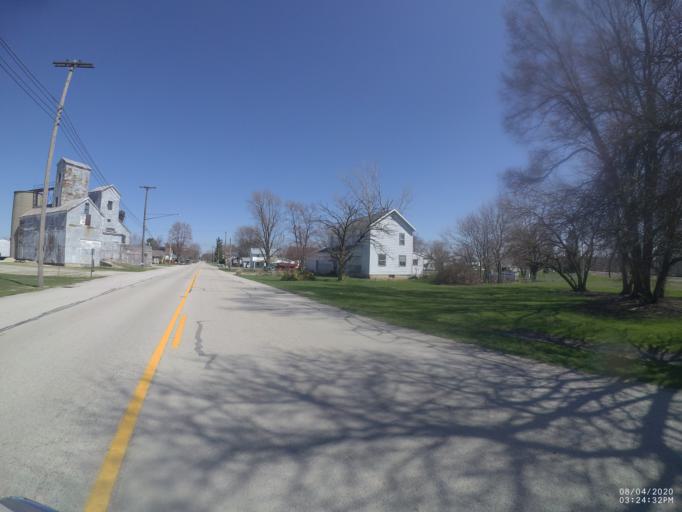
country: US
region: Ohio
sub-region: Sandusky County
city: Stony Prairie
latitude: 41.2676
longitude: -83.2495
